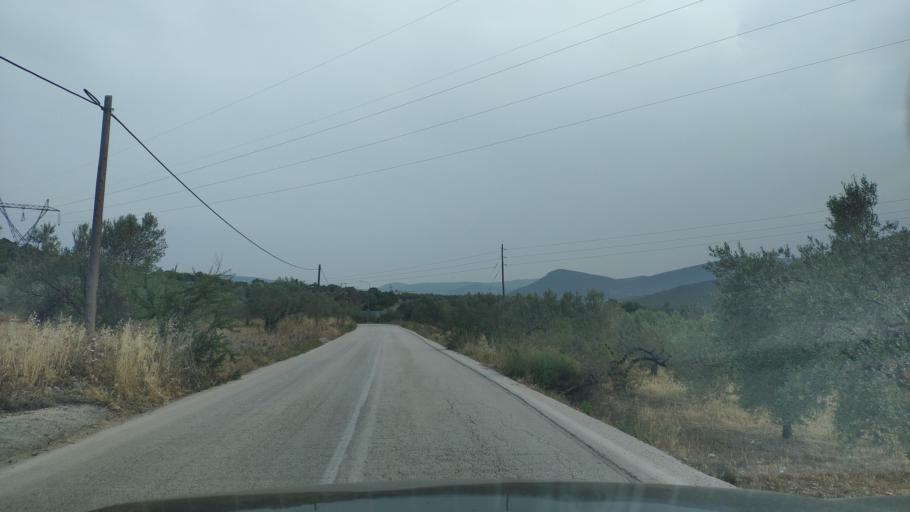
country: GR
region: Peloponnese
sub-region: Nomos Argolidos
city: Palaia Epidavros
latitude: 37.5728
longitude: 23.1494
